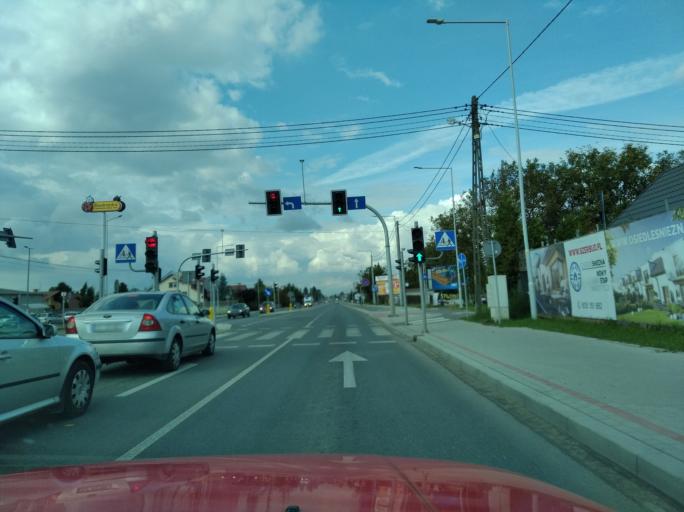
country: PL
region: Subcarpathian Voivodeship
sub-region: Powiat rzeszowski
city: Tyczyn
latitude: 49.9671
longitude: 22.0296
